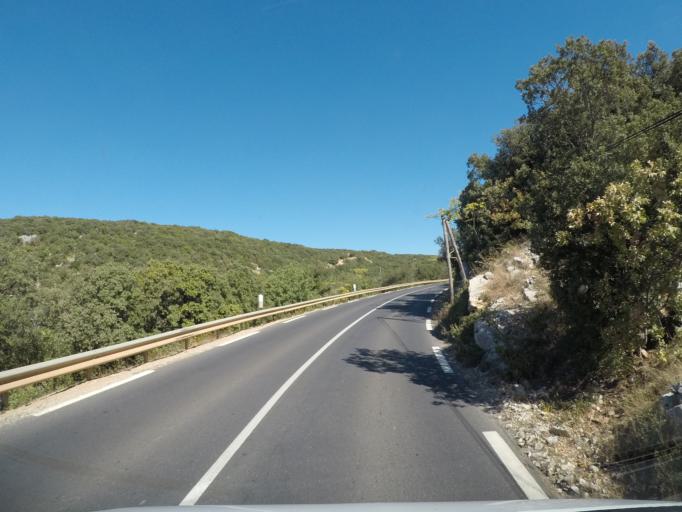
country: FR
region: Languedoc-Roussillon
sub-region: Departement de l'Herault
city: Aniane
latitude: 43.7250
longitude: 3.6285
